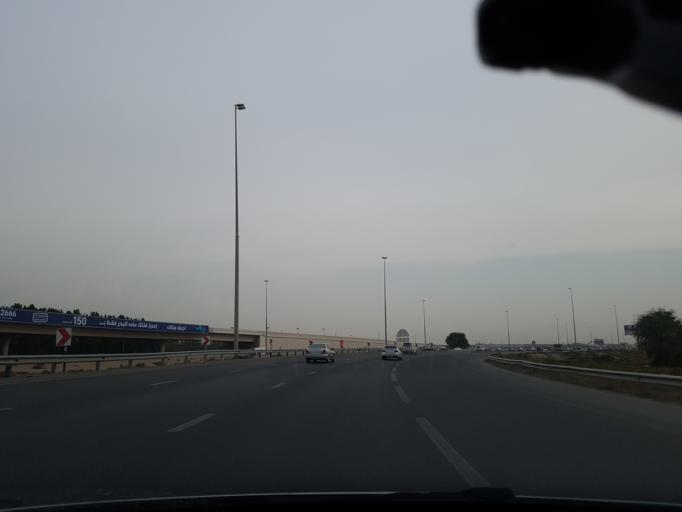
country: AE
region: Ajman
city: Ajman
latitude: 25.3579
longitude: 55.4808
